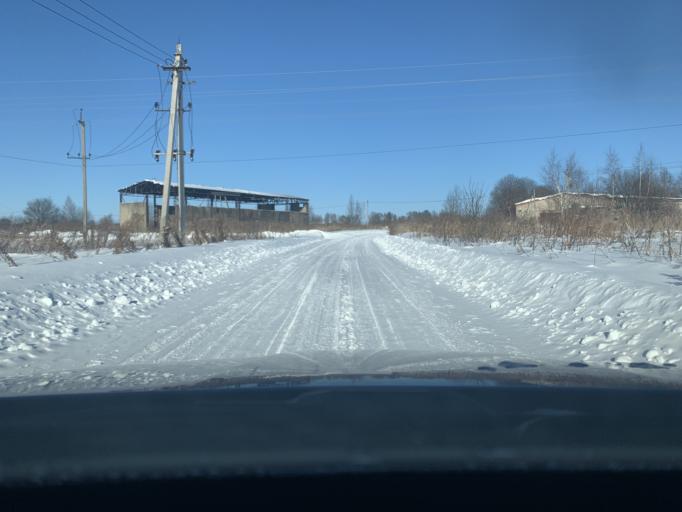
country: RU
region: Jaroslavl
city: Tunoshna
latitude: 57.6535
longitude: 40.0677
